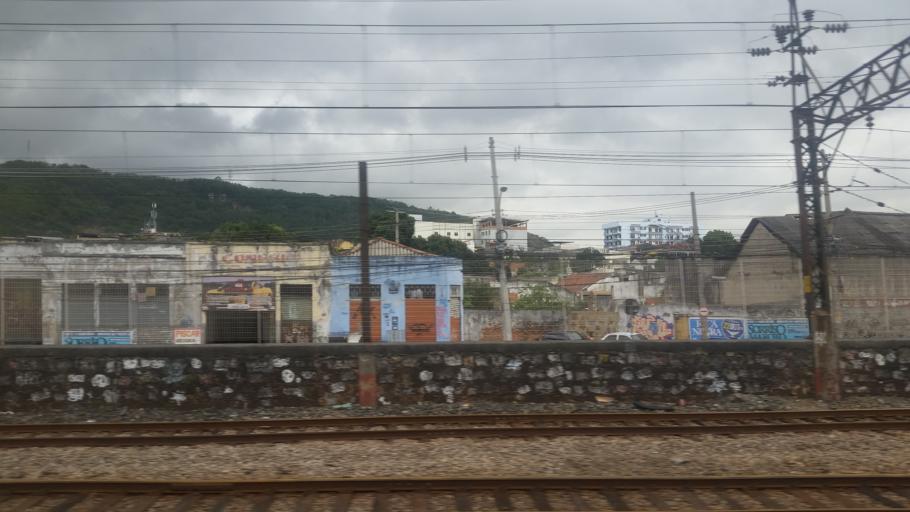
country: BR
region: Rio de Janeiro
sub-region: Sao Joao De Meriti
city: Sao Joao de Meriti
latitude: -22.8817
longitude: -43.3290
